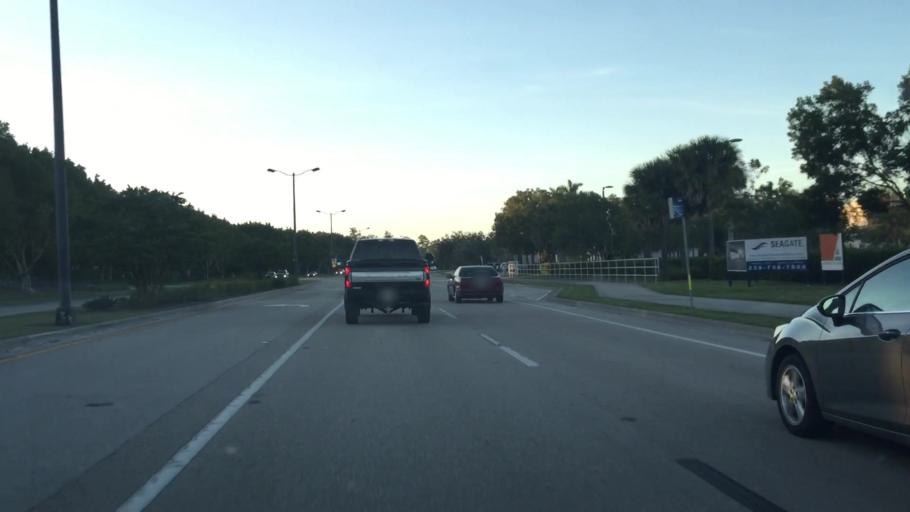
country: US
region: Florida
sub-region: Lee County
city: Three Oaks
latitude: 26.4563
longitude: -81.7796
